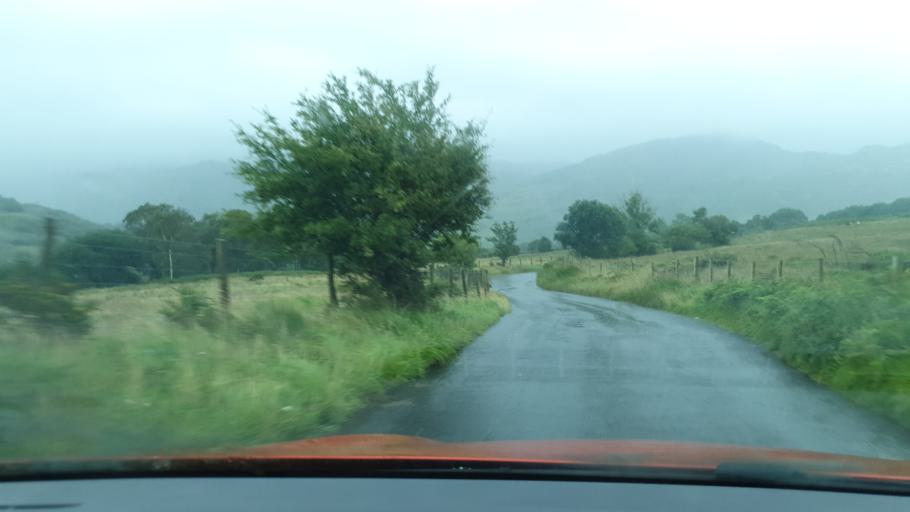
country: GB
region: England
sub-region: Cumbria
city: Millom
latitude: 54.3363
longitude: -3.2420
